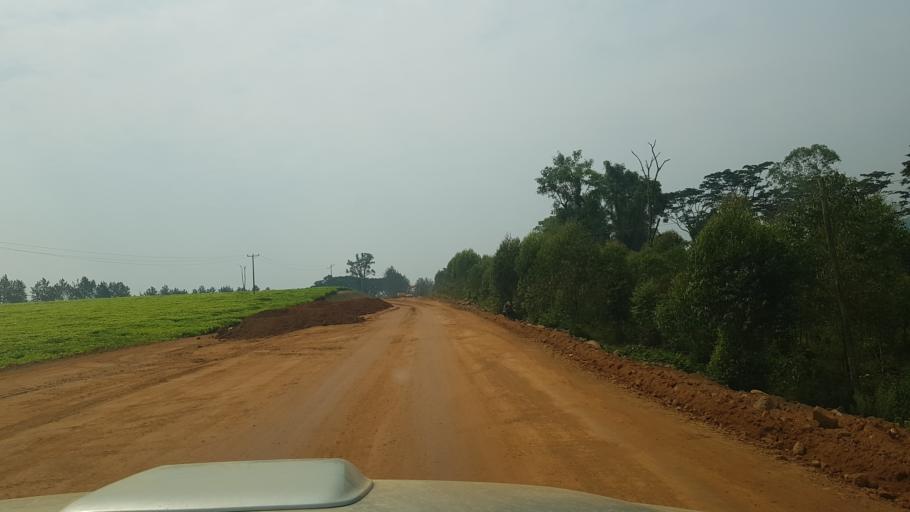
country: ET
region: Oromiya
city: Gore
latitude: 7.8487
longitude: 35.4763
